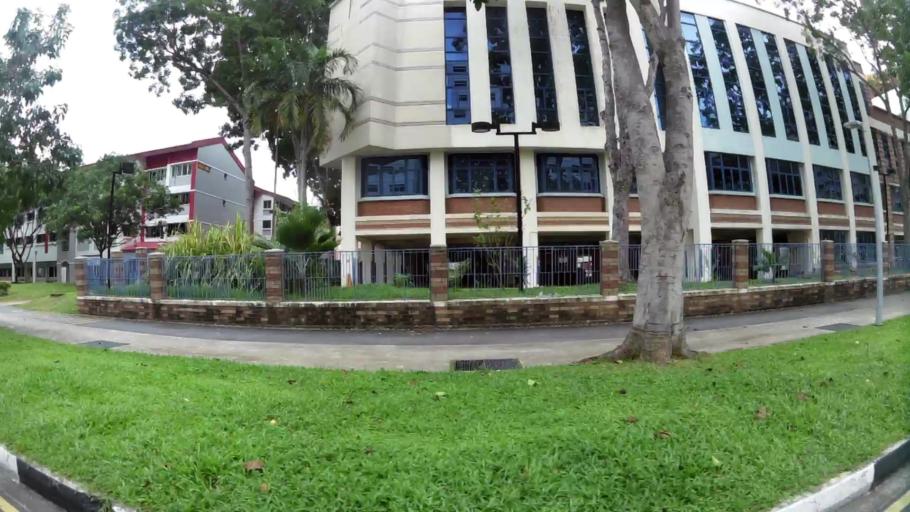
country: SG
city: Singapore
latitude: 1.3617
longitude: 103.9519
